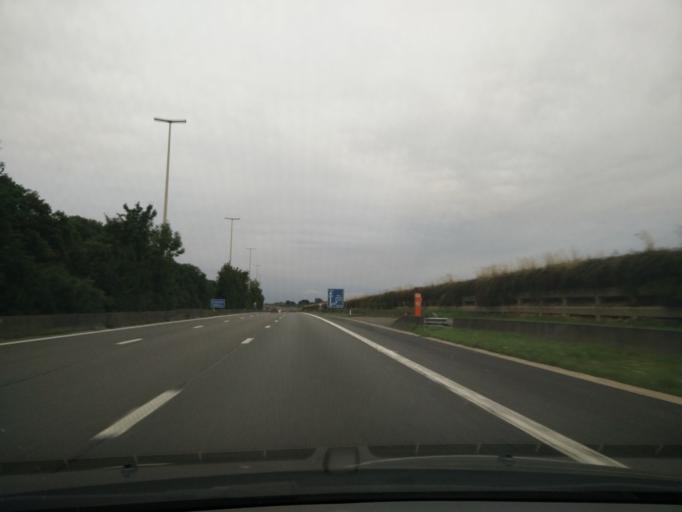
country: BE
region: Wallonia
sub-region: Province de Liege
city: Lincent
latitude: 50.7179
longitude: 5.0129
